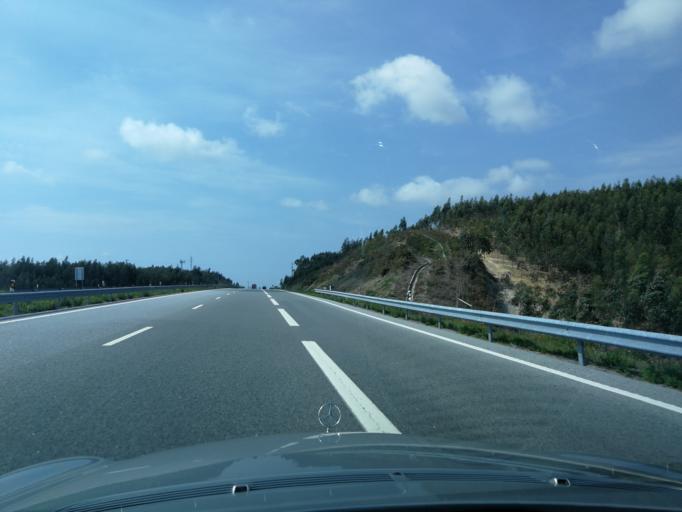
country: PT
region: Braga
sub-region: Vila Nova de Famalicao
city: Ribeirao
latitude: 41.3785
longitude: -8.5700
